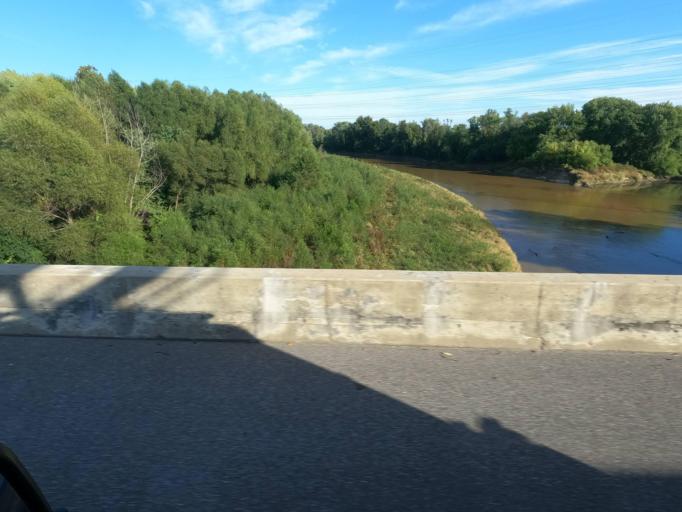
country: US
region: Tennessee
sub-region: Shelby County
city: Memphis
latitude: 35.1871
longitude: -90.0168
